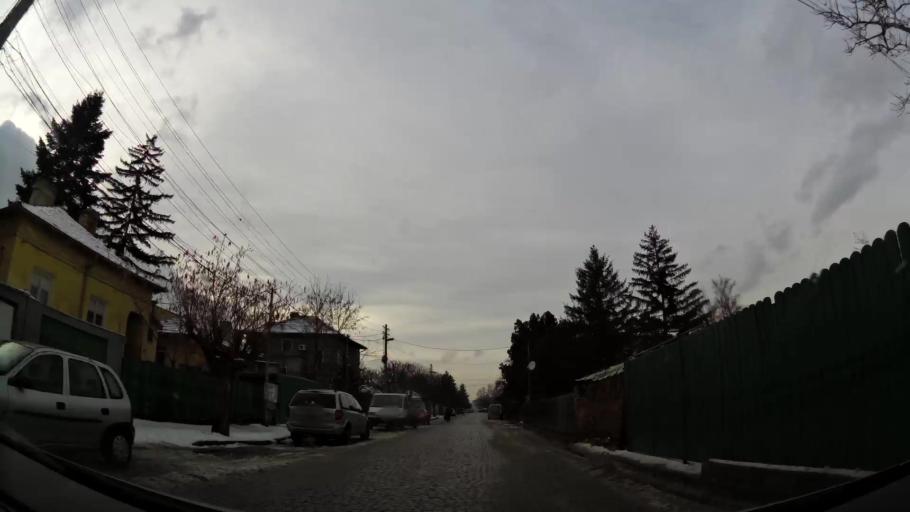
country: BG
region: Sofia-Capital
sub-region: Stolichna Obshtina
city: Sofia
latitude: 42.7212
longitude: 23.3395
